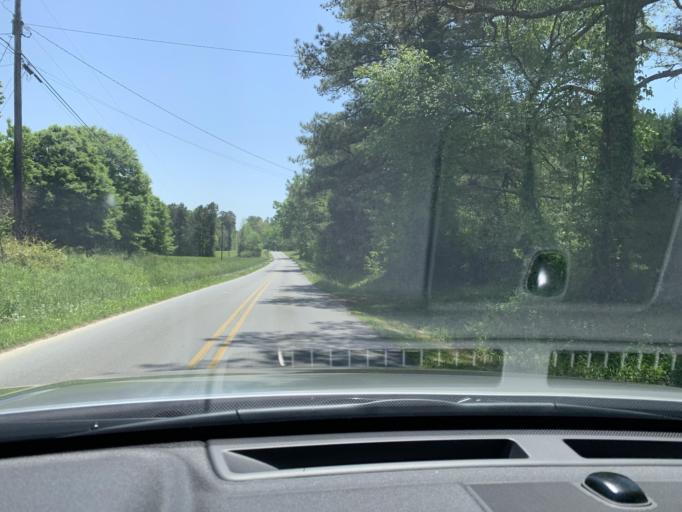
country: US
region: Georgia
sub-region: Polk County
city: Aragon
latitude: 34.0840
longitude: -85.1206
